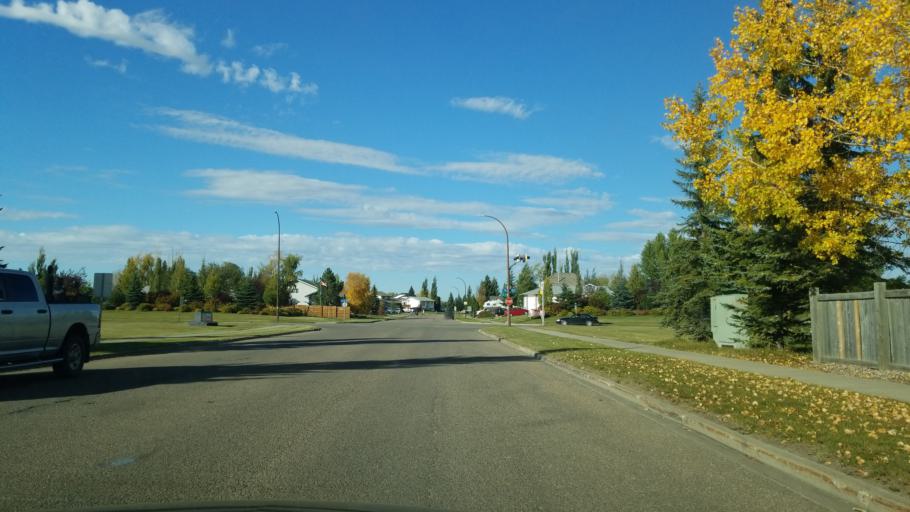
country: CA
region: Saskatchewan
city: Lloydminster
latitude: 53.2590
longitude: -110.0237
